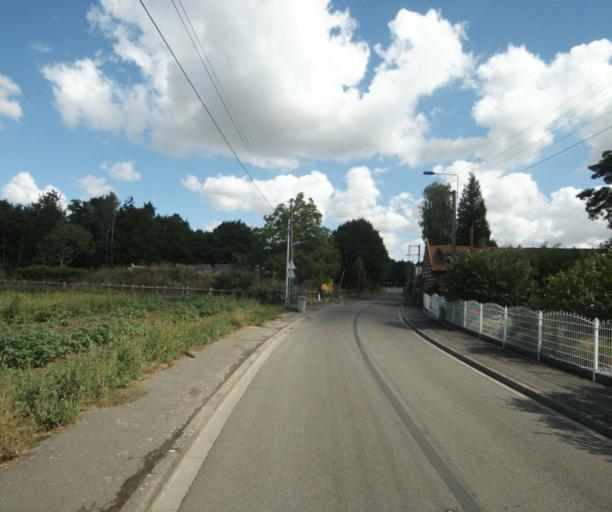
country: FR
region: Nord-Pas-de-Calais
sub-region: Departement du Nord
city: Willems
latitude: 50.6282
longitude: 3.2307
